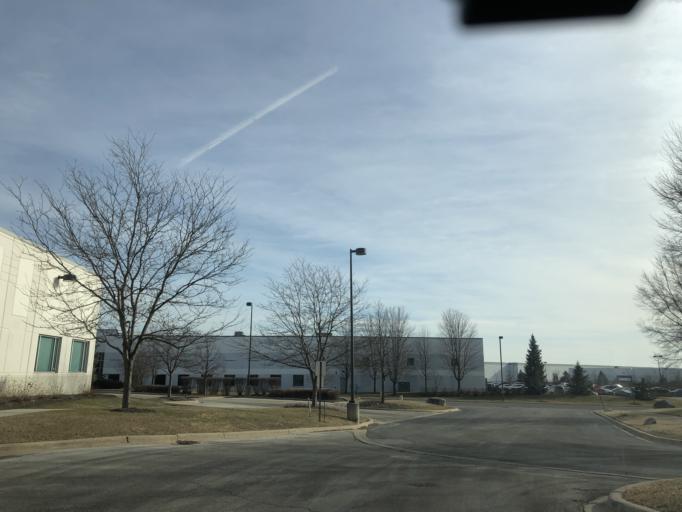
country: US
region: Illinois
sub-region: Cook County
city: Lemont
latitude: 41.7015
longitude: -88.0252
